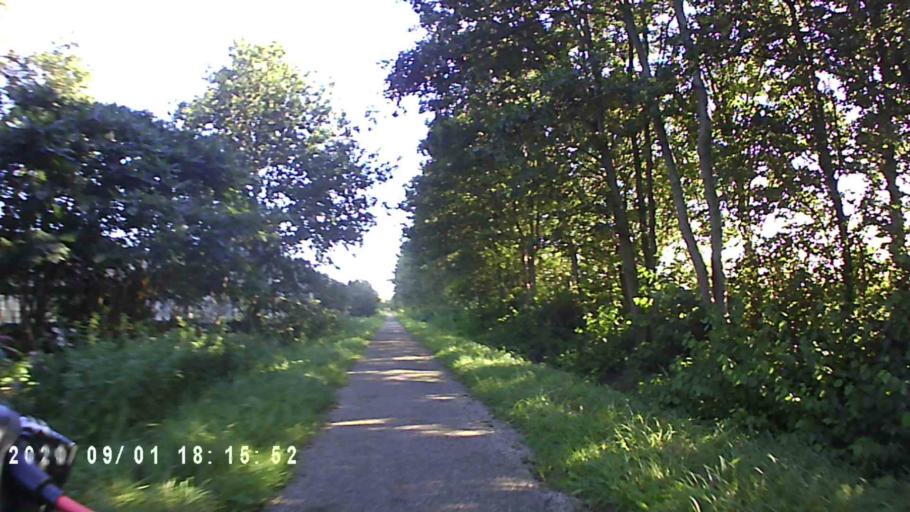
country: NL
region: Groningen
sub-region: Gemeente Hoogezand-Sappemeer
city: Sappemeer
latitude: 53.1784
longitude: 6.7859
